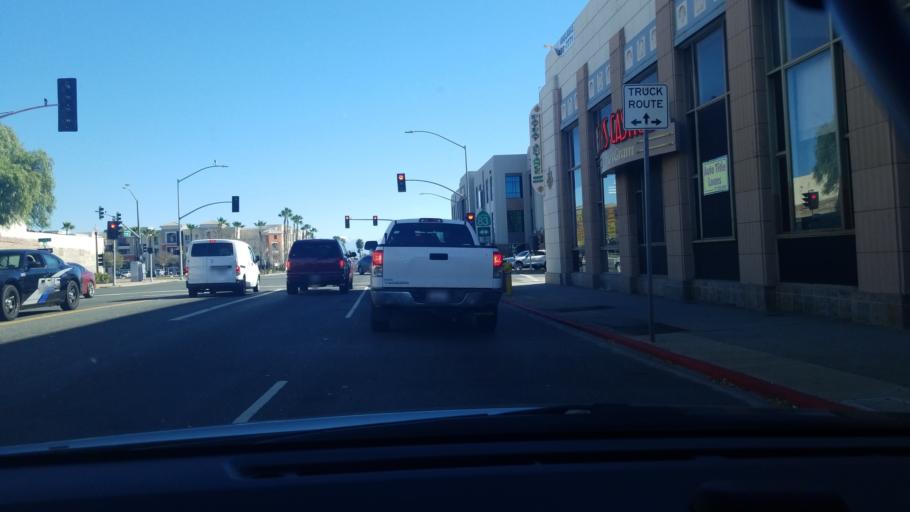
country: US
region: California
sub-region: San Bernardino County
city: Ontario
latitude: 34.0633
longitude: -117.6516
